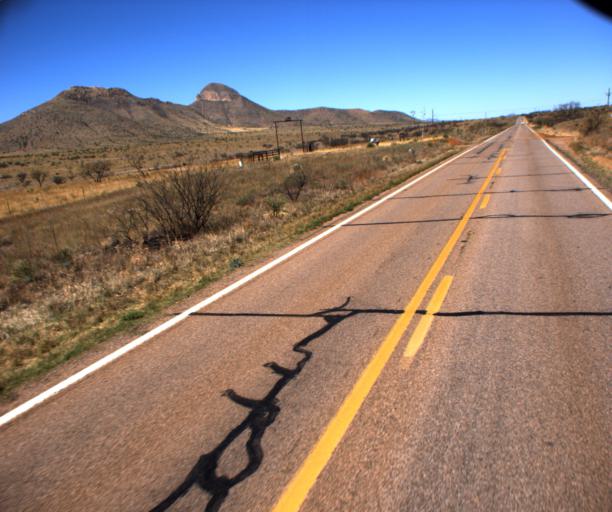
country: US
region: Arizona
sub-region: Cochise County
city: Huachuca City
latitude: 31.7126
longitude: -110.4569
